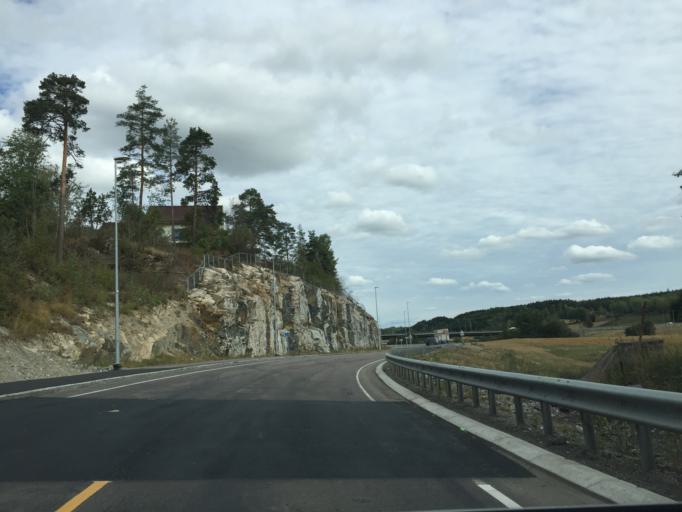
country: NO
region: Ostfold
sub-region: Hobol
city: Elvestad
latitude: 59.6242
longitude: 10.9523
